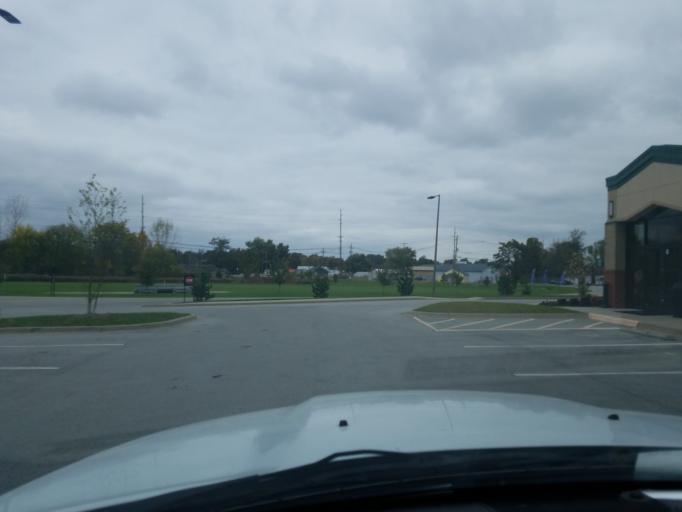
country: US
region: Kentucky
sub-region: Jefferson County
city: Pleasure Ridge Park
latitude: 38.1420
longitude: -85.8358
